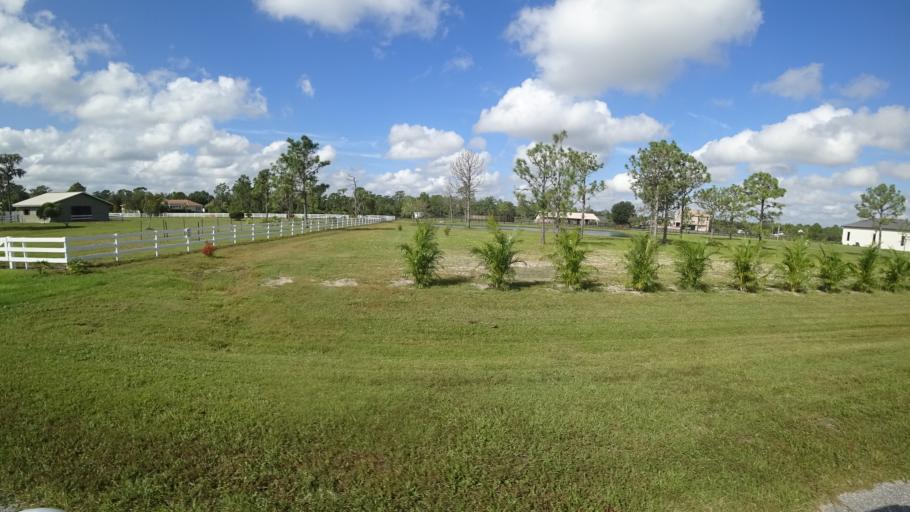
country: US
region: Florida
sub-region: Sarasota County
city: The Meadows
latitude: 27.4004
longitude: -82.3326
